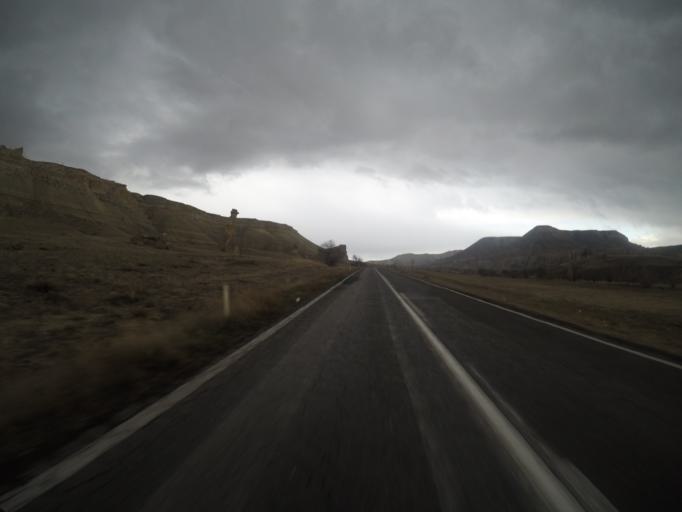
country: TR
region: Nevsehir
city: Avanos
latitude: 38.6812
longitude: 34.8413
